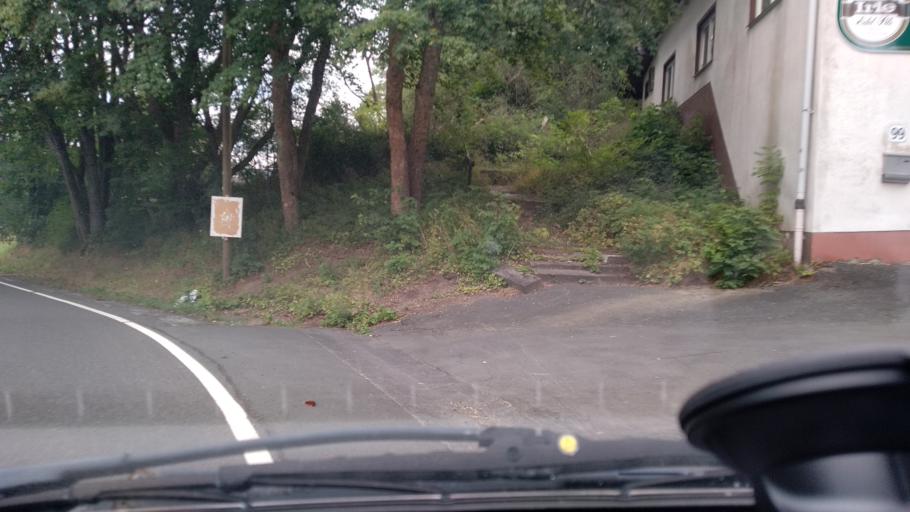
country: DE
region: Hesse
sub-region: Regierungsbezirk Giessen
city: Haiger
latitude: 50.8528
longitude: 8.2194
